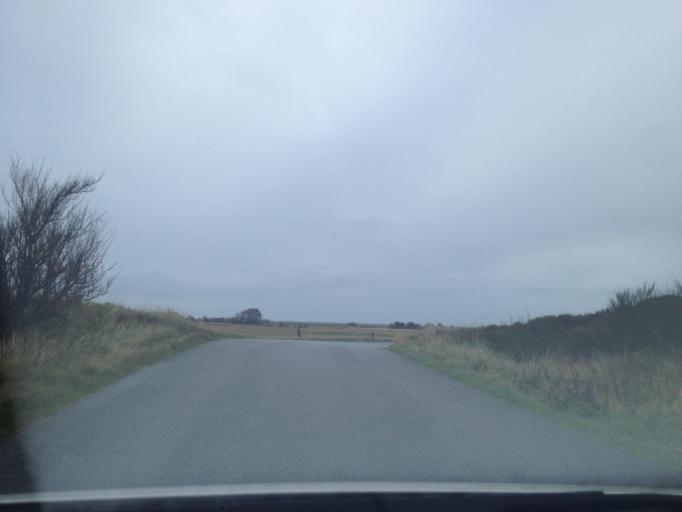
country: DE
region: Schleswig-Holstein
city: List
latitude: 55.1587
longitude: 8.5447
